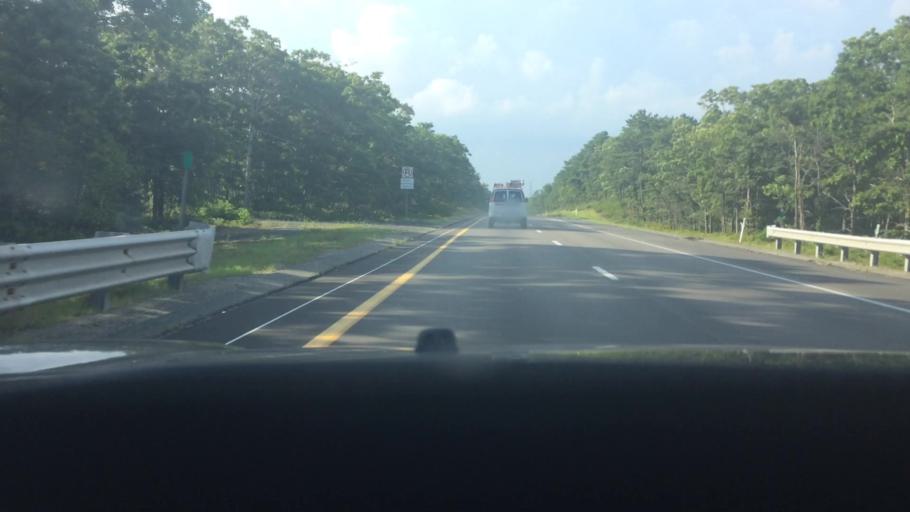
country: US
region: Massachusetts
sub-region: Plymouth County
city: Plymouth
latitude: 41.8960
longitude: -70.6141
